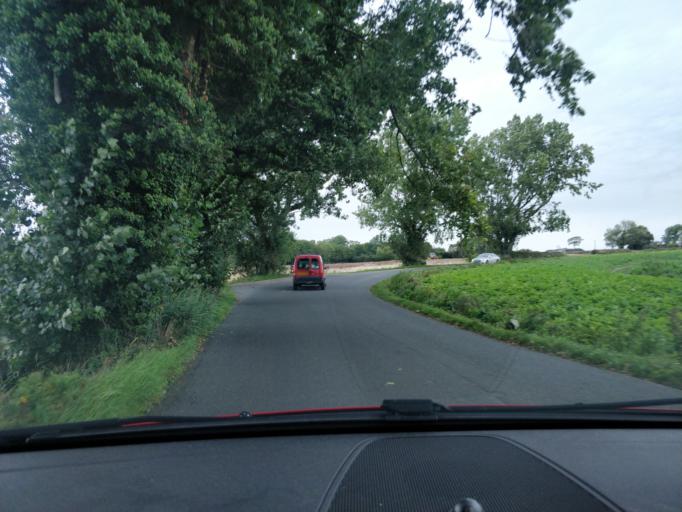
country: GB
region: England
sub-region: Lancashire
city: Ormskirk
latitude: 53.6178
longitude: -2.8593
